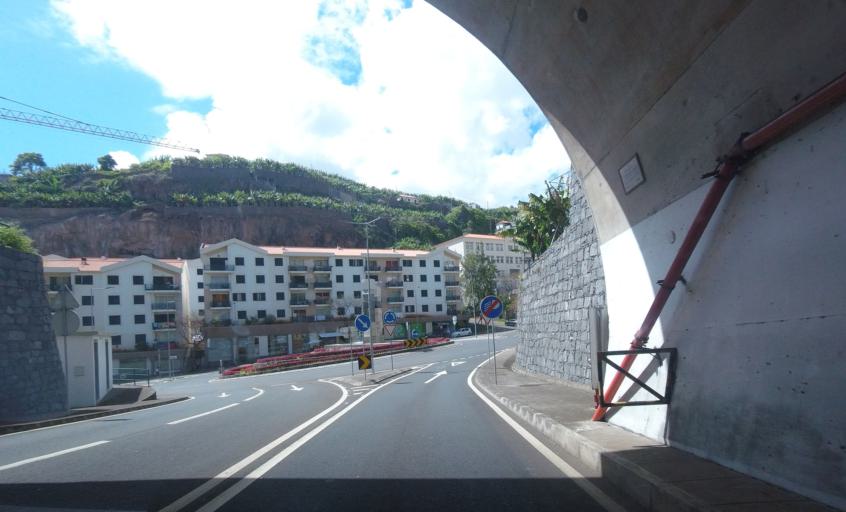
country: PT
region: Madeira
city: Camara de Lobos
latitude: 32.6532
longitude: -16.9784
